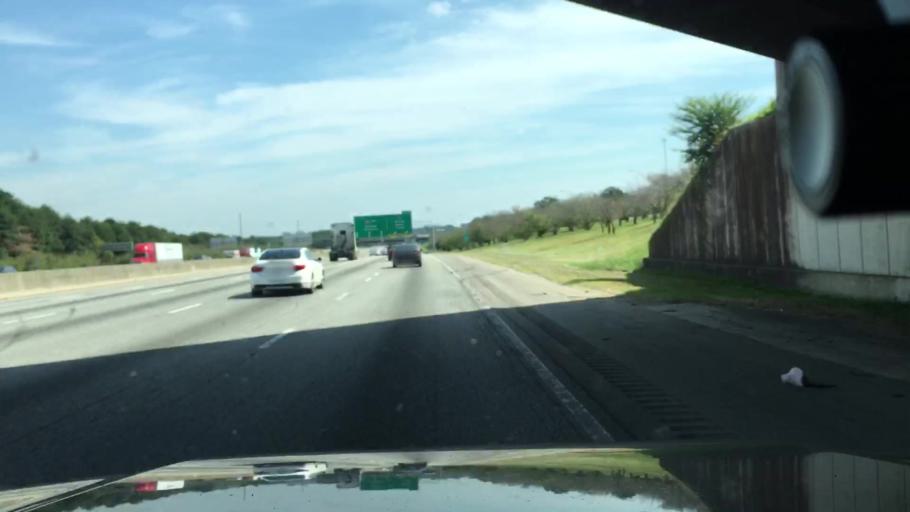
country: US
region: Georgia
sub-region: Fulton County
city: Hapeville
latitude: 33.6249
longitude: -84.4218
